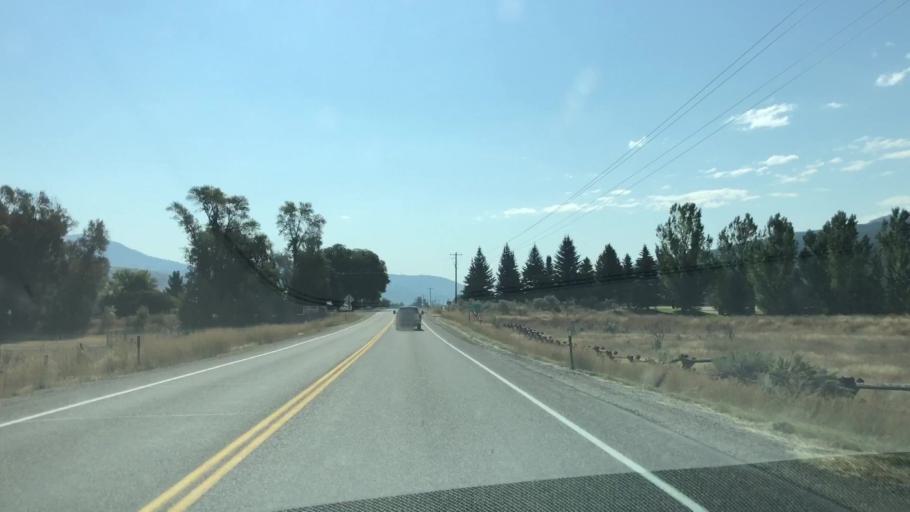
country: US
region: Idaho
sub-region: Teton County
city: Victor
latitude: 43.4015
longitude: -111.2882
